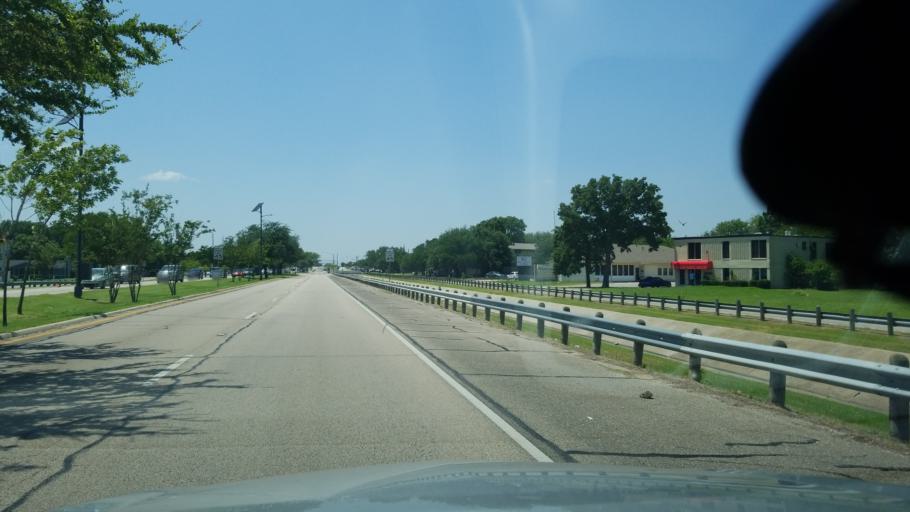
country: US
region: Texas
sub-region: Dallas County
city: Irving
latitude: 32.8266
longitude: -96.9708
